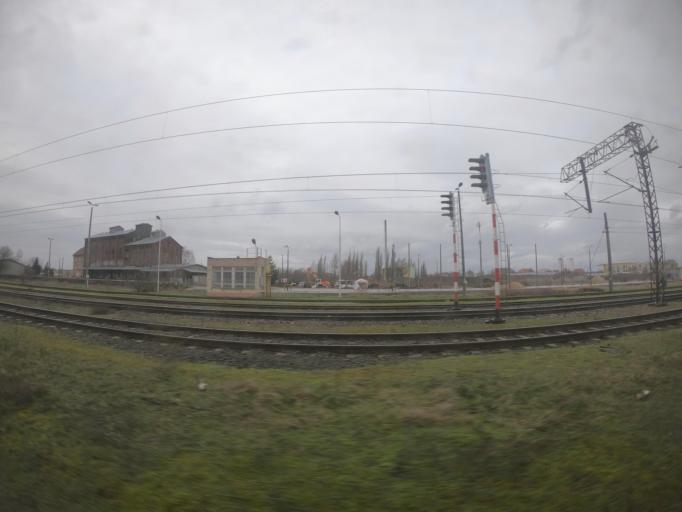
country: PL
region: West Pomeranian Voivodeship
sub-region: Powiat szczecinecki
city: Szczecinek
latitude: 53.6972
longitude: 16.7111
